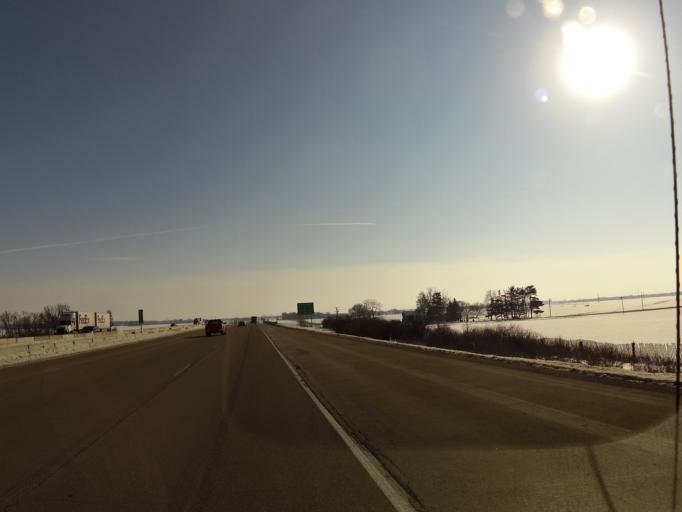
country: US
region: Wisconsin
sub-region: Rock County
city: Beloit
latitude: 42.5862
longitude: -88.9819
